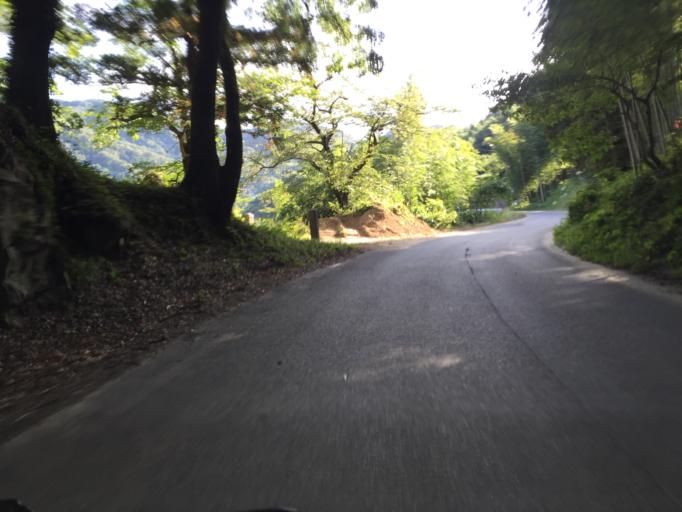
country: JP
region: Fukushima
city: Yanagawamachi-saiwaicho
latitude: 37.9063
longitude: 140.6613
